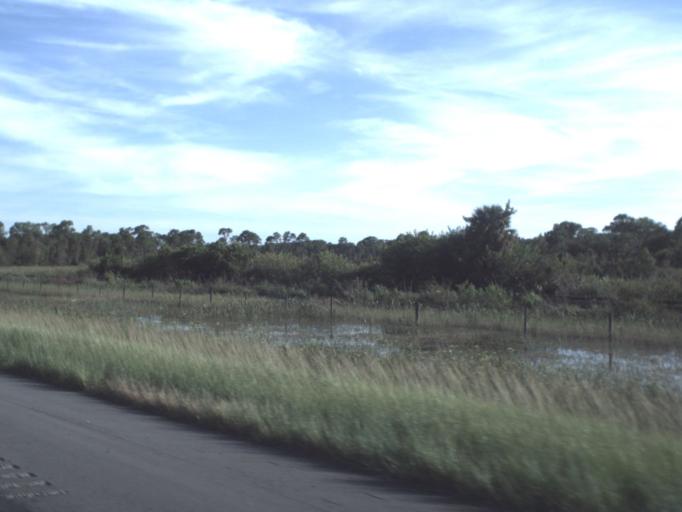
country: US
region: Florida
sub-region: Lee County
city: Suncoast Estates
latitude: 26.8091
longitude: -81.9305
